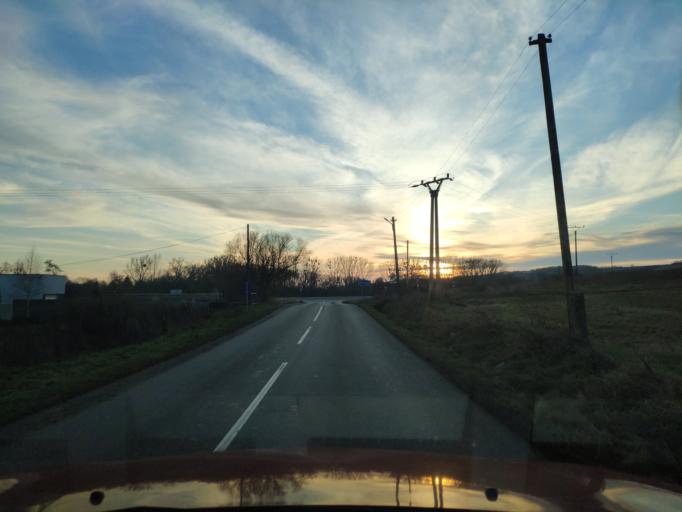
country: SK
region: Kosicky
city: Kosice
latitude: 48.6609
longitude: 21.3924
